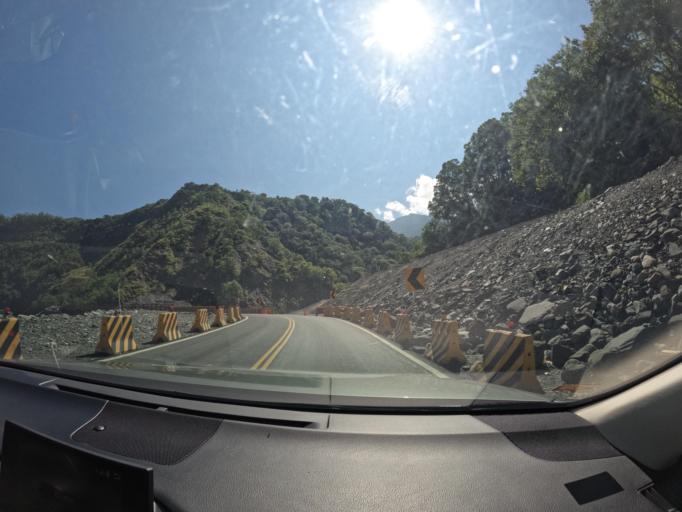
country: TW
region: Taiwan
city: Yujing
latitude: 23.1875
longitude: 120.7867
